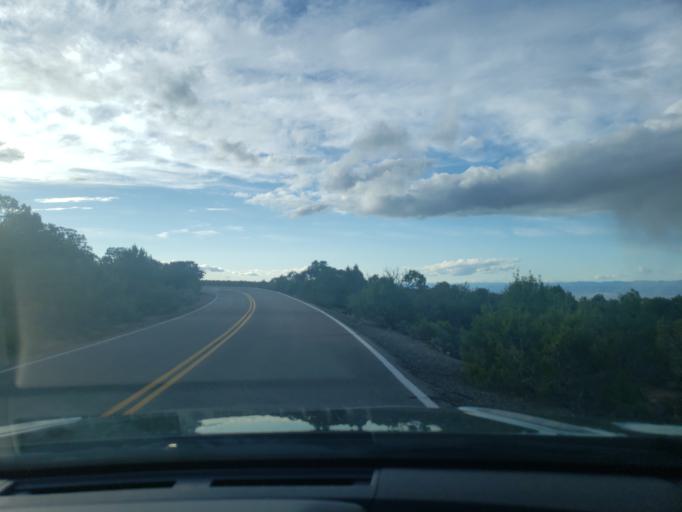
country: US
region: Colorado
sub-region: Mesa County
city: Redlands
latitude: 39.0325
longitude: -108.6604
